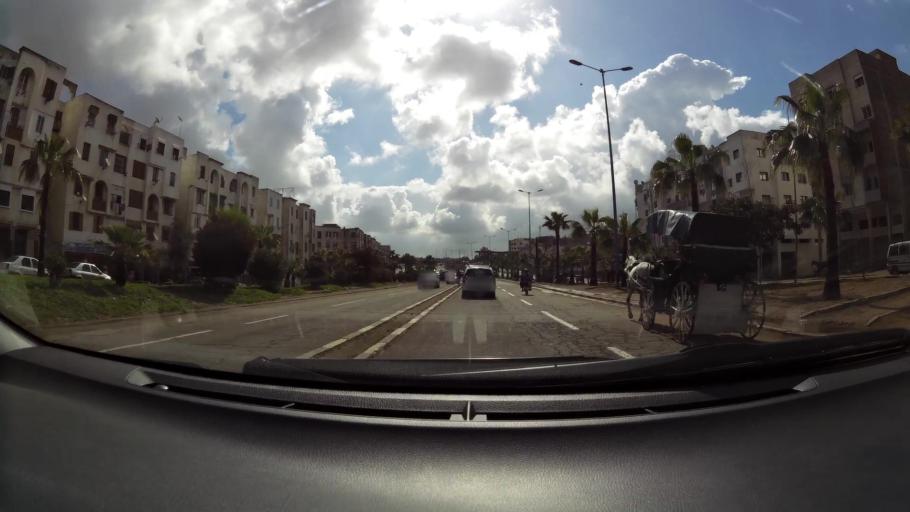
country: MA
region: Grand Casablanca
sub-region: Mediouna
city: Tit Mellil
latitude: 33.5707
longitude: -7.5233
